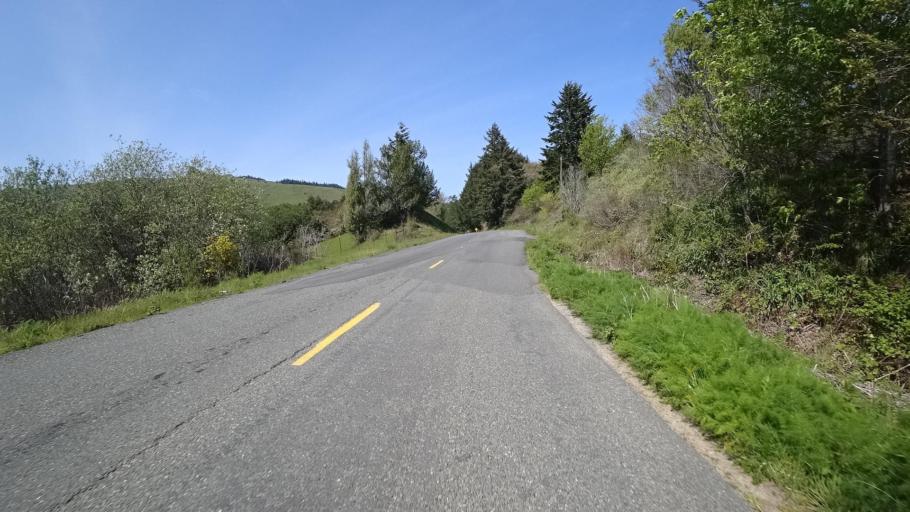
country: US
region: California
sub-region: Humboldt County
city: Rio Dell
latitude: 40.4620
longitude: -123.8048
